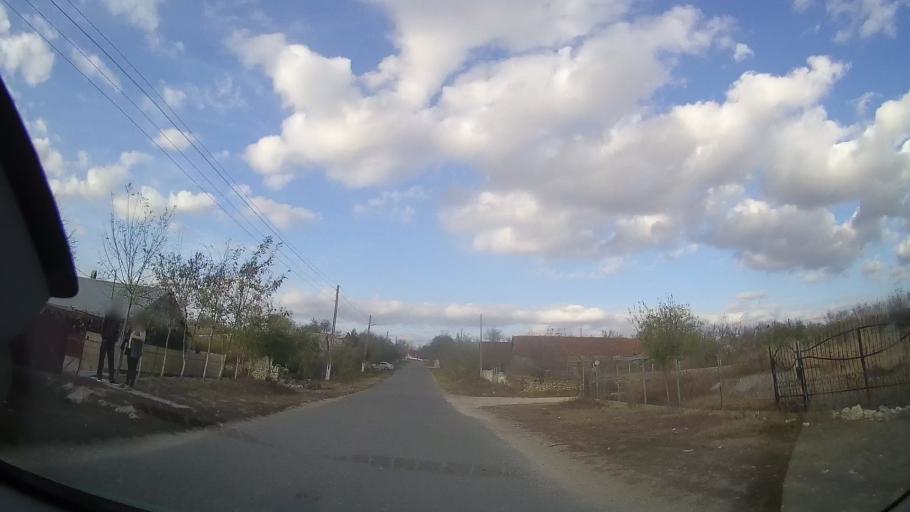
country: RO
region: Constanta
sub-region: Comuna Cerchezu
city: Cerchezu
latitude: 43.8586
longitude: 28.1013
